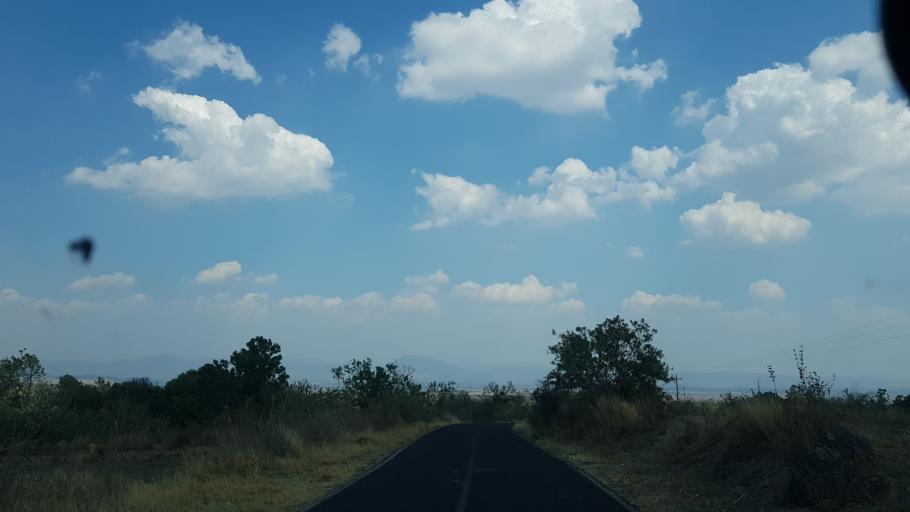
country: MX
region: Puebla
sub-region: Atlixco
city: San Pedro Benito Juarez
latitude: 18.9452
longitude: -98.5361
